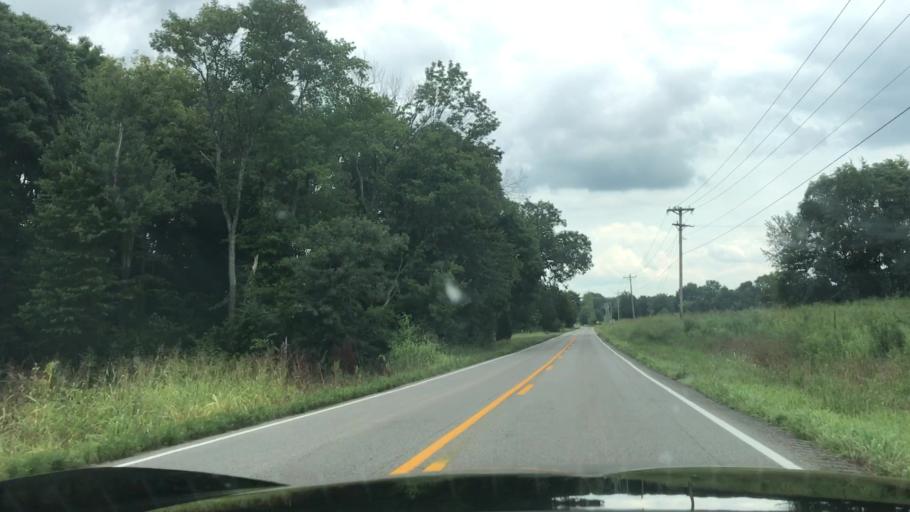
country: US
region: Kentucky
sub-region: Muhlenberg County
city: Central City
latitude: 37.1978
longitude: -86.9986
